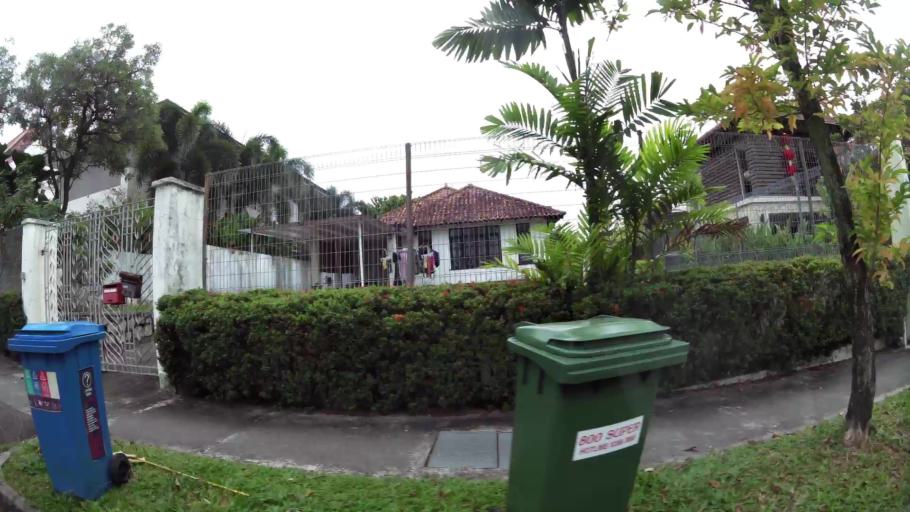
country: SG
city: Singapore
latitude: 1.3592
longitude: 103.8614
